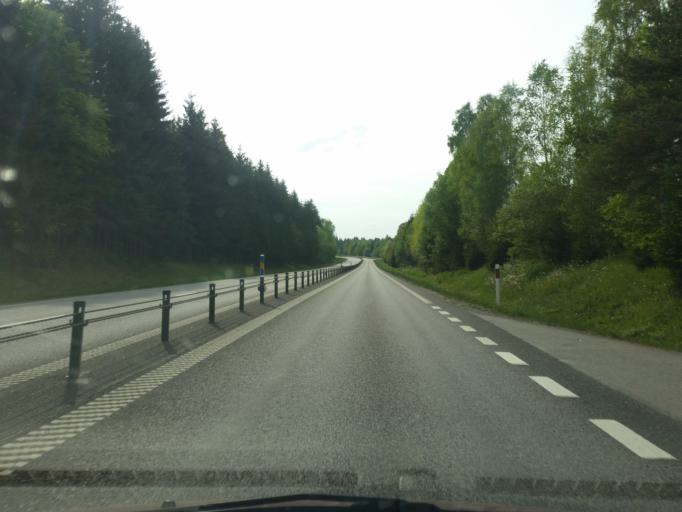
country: SE
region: Vaestra Goetaland
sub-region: Ulricehamns Kommun
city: Ulricehamn
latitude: 57.8016
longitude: 13.3581
